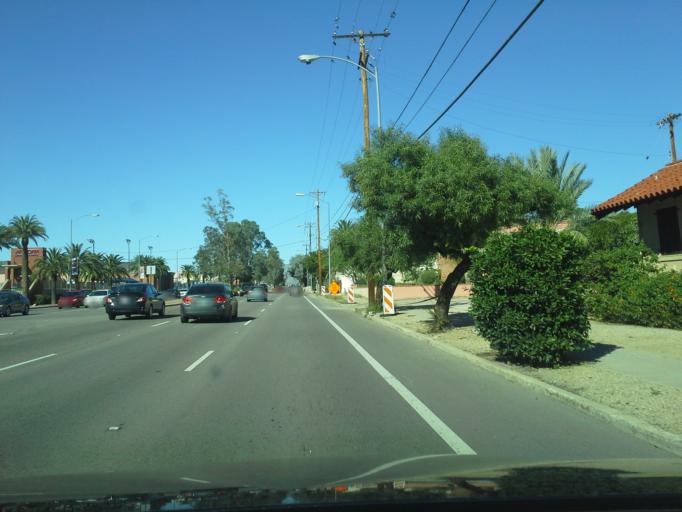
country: US
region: Arizona
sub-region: Pima County
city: Tucson
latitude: 32.2293
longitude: -110.9438
